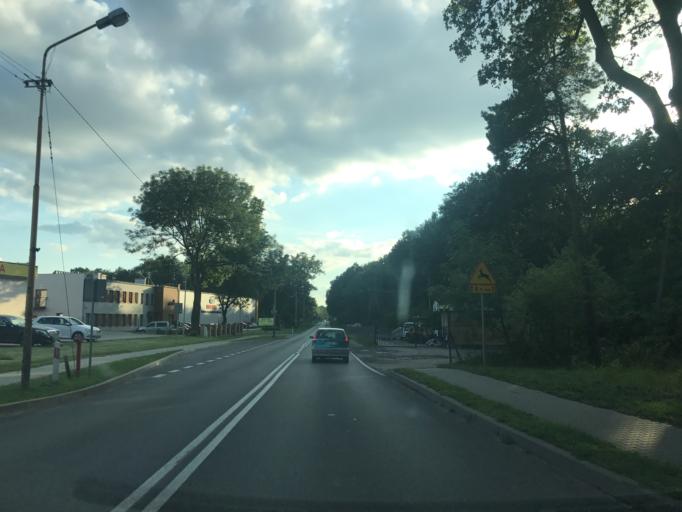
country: PL
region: Greater Poland Voivodeship
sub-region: Powiat jarocinski
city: Jarocin
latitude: 51.9701
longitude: 17.4835
